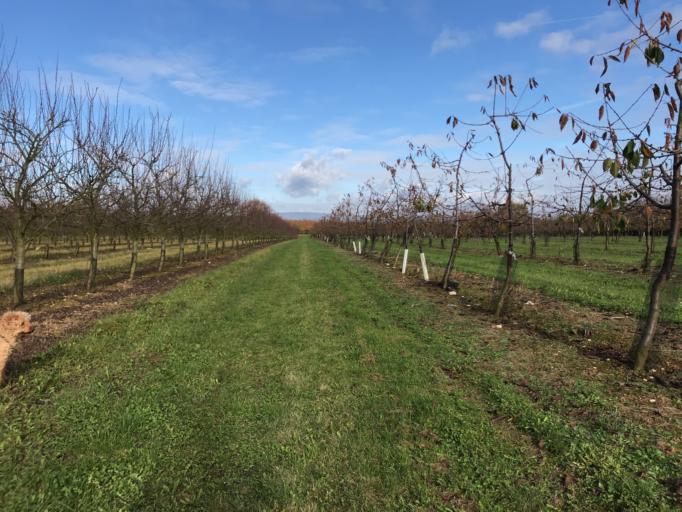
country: DE
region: Rheinland-Pfalz
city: Budenheim
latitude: 49.9920
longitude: 8.1477
